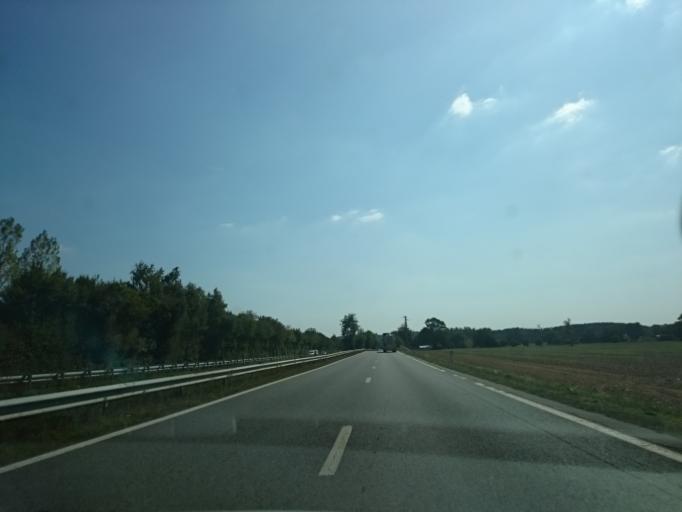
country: FR
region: Brittany
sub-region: Departement d'Ille-et-Vilaine
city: Bain-de-Bretagne
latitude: 47.8161
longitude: -1.6896
